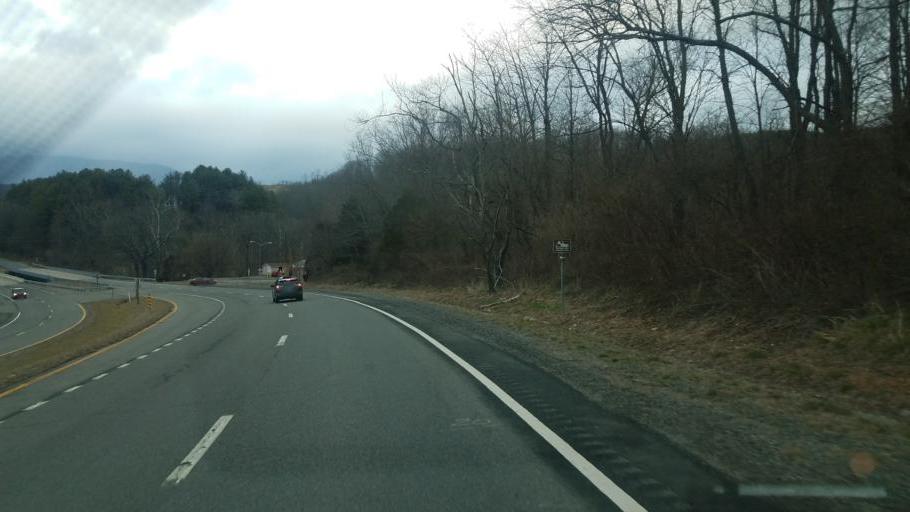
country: US
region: Virginia
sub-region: Giles County
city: Pearisburg
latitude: 37.2652
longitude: -80.7100
